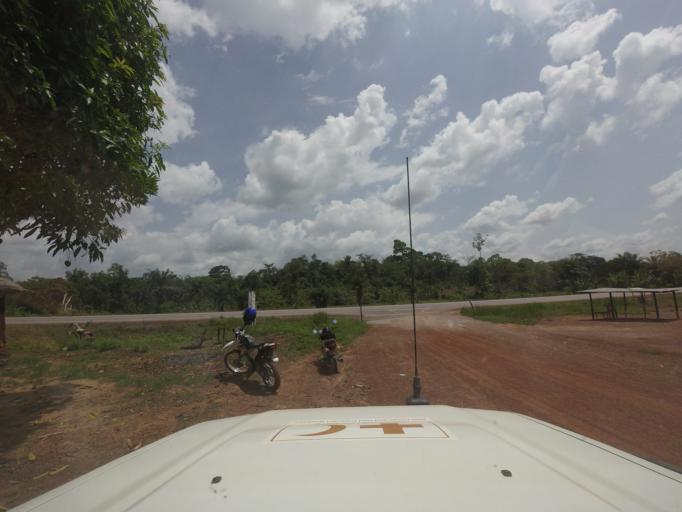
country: LR
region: Bong
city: Gbarnga
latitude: 7.0512
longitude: -9.2375
